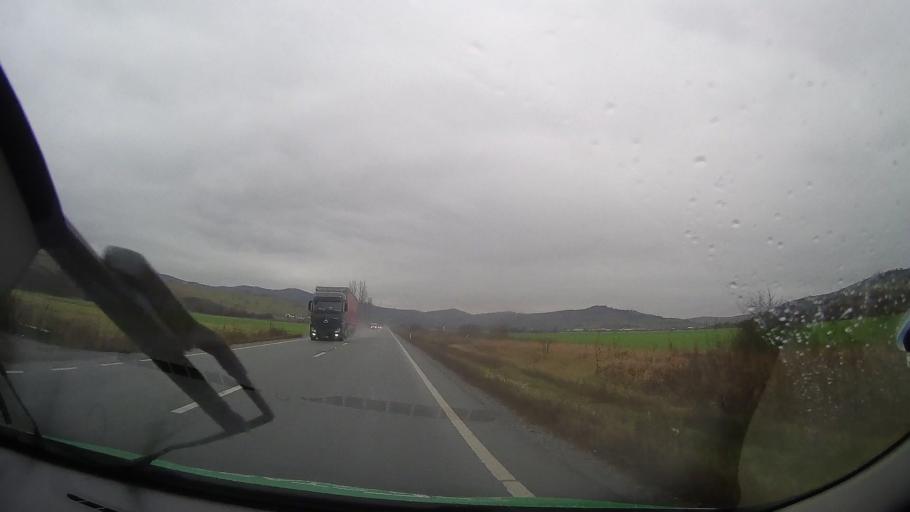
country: RO
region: Bistrita-Nasaud
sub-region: Comuna Teaca
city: Teaca
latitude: 46.9251
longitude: 24.4871
